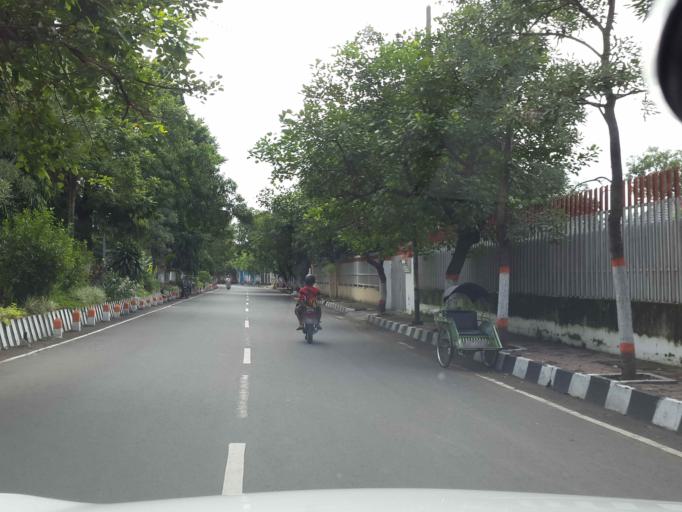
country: ID
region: East Java
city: Mojokerto
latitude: -7.4610
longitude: 112.4322
